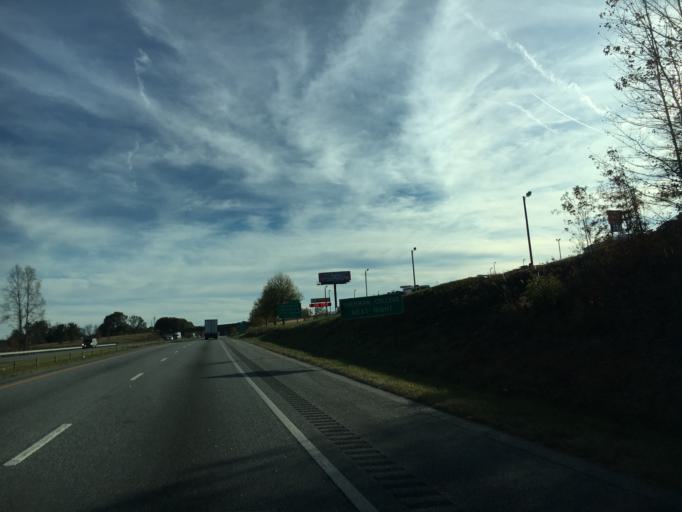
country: US
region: South Carolina
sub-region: Spartanburg County
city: Boiling Springs
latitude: 35.0315
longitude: -82.0354
